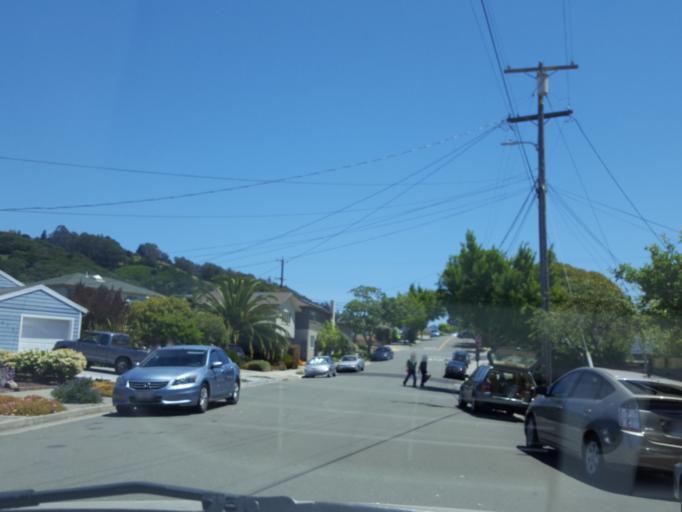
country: US
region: California
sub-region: Contra Costa County
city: El Cerrito
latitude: 37.9234
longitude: -122.3104
